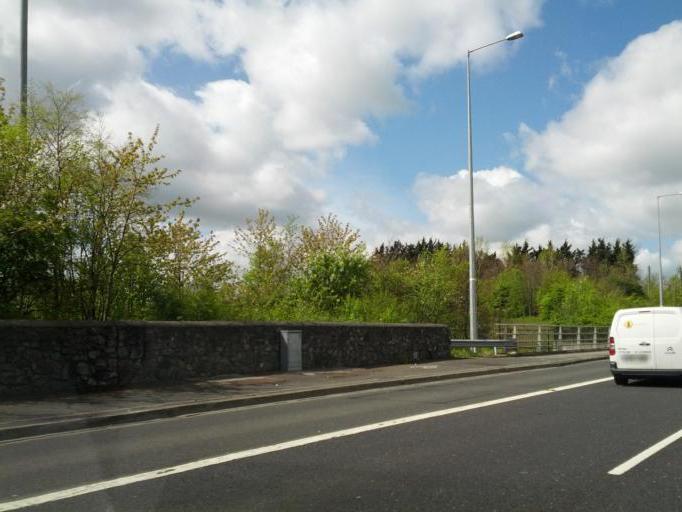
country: IE
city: Palmerstown
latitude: 53.3565
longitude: -6.4015
